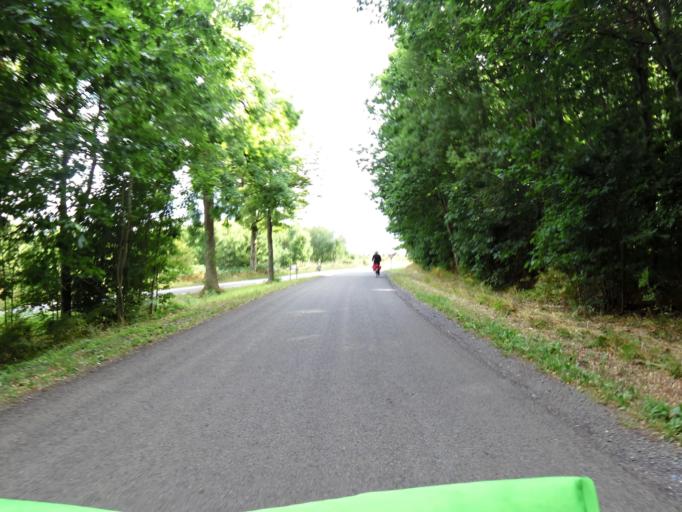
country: BE
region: Wallonia
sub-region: Province de Namur
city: Bievre
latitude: 49.9185
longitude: 5.0022
